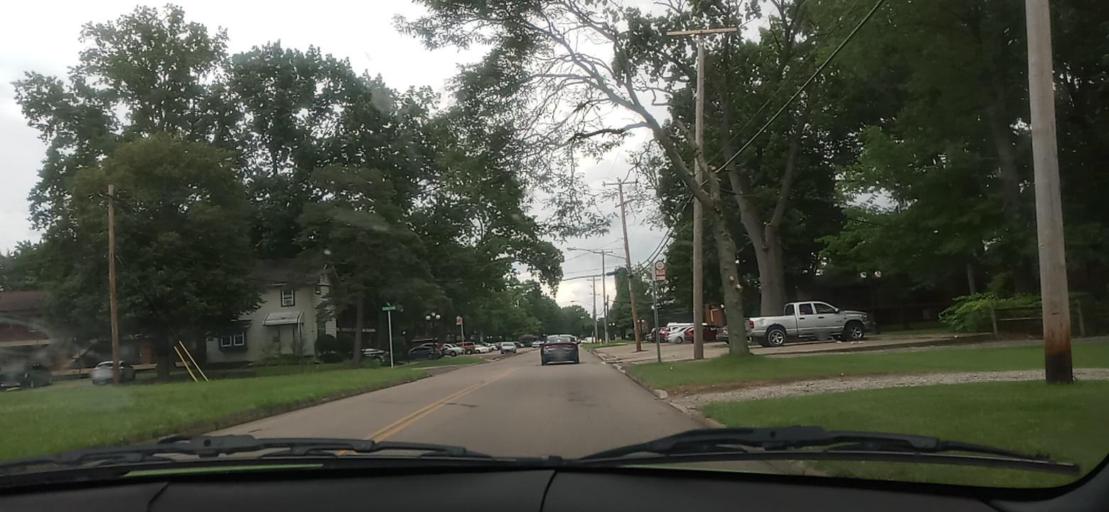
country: US
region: Ohio
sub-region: Summit County
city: Portage Lakes
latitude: 41.0247
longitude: -81.5562
